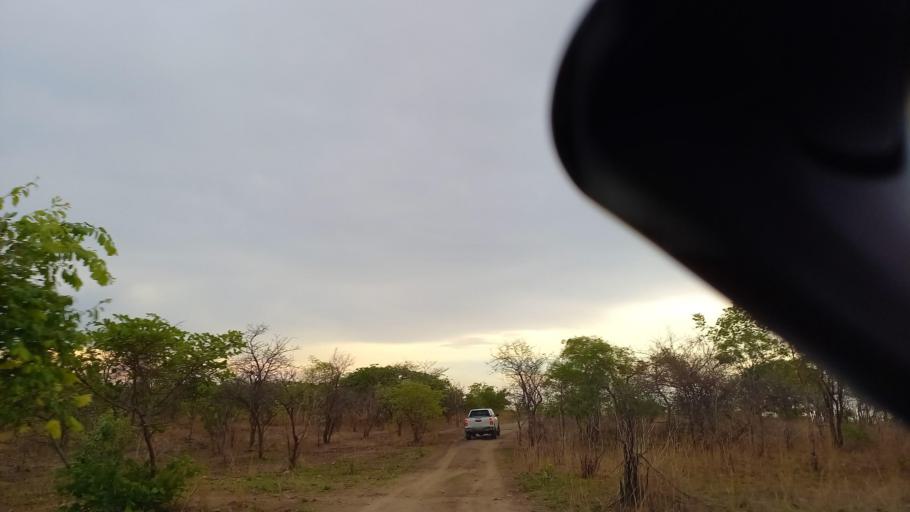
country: ZM
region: Lusaka
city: Kafue
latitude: -16.0480
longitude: 28.3232
